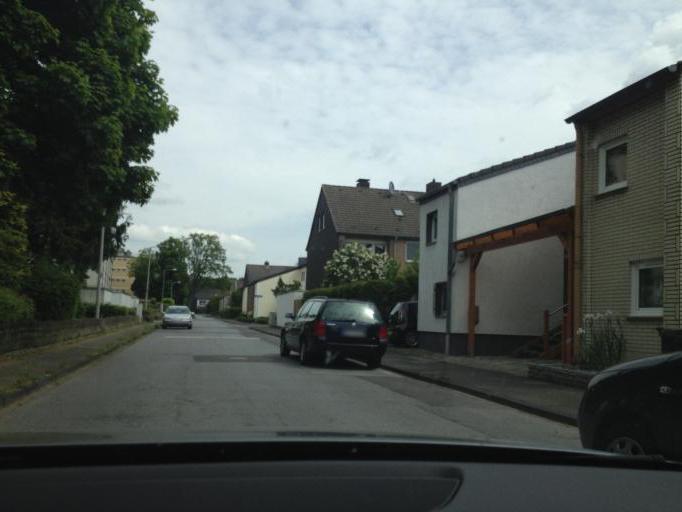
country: DE
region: North Rhine-Westphalia
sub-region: Regierungsbezirk Dusseldorf
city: Hochfeld
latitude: 51.3721
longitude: 6.7677
